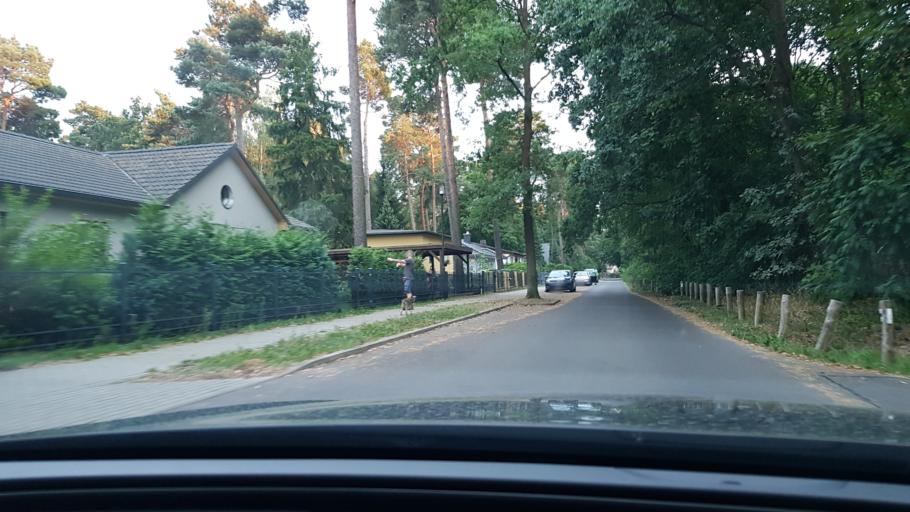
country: DE
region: Berlin
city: Mahlsdorf
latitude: 52.4830
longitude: 13.6286
